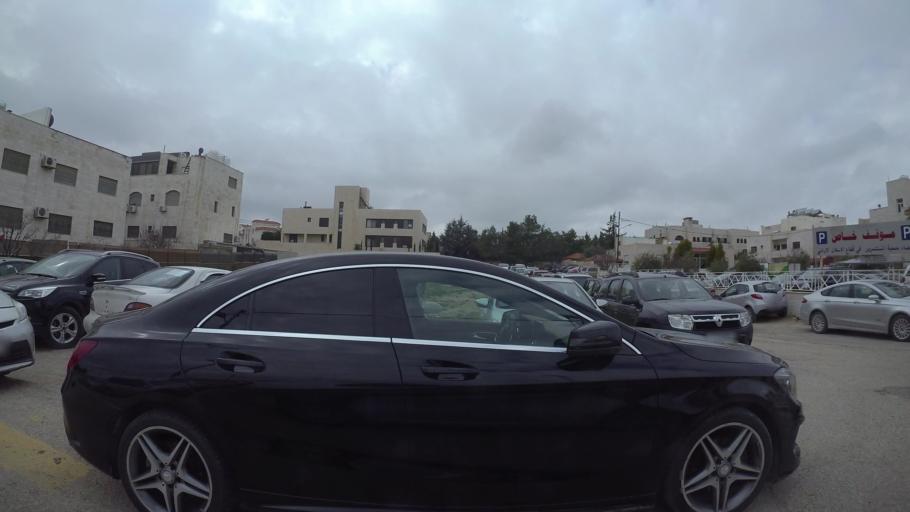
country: JO
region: Amman
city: Wadi as Sir
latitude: 31.9860
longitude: 35.8355
